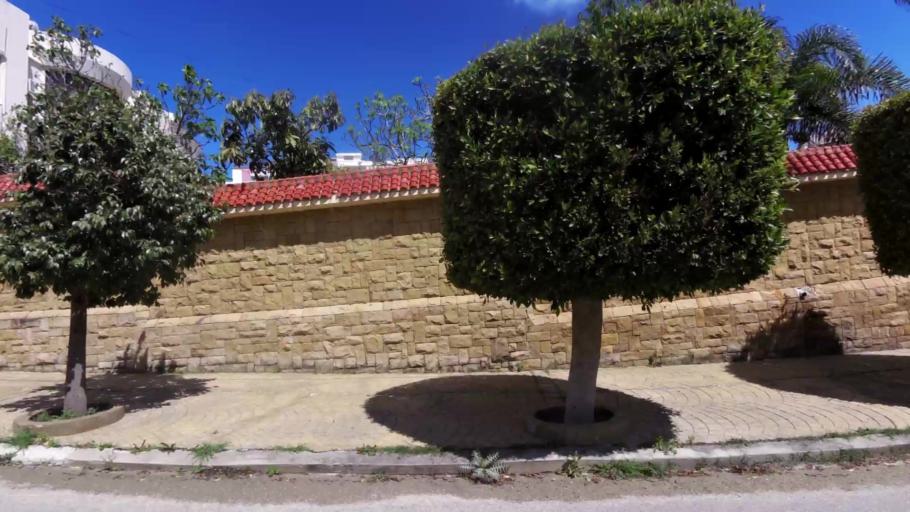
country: MA
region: Tanger-Tetouan
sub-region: Tanger-Assilah
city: Tangier
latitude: 35.7700
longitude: -5.8375
